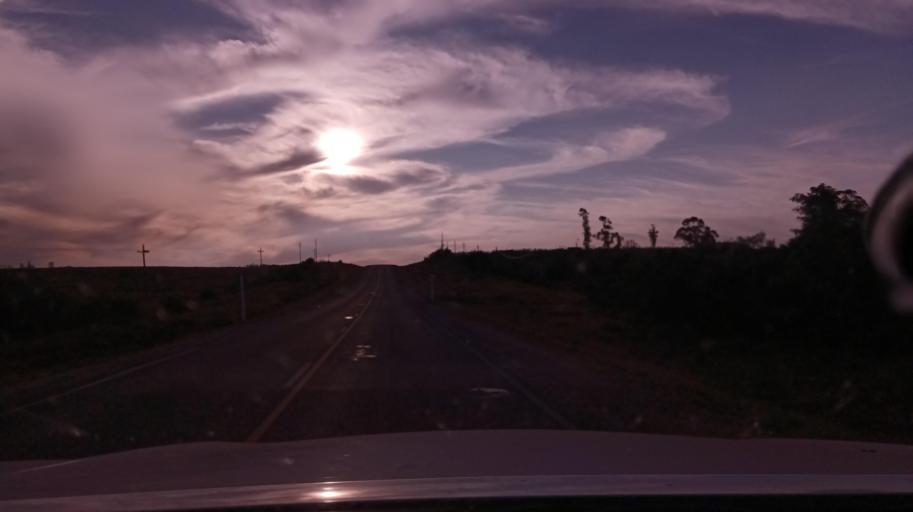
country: UY
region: Canelones
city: San Ramon
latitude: -34.1812
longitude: -56.0701
